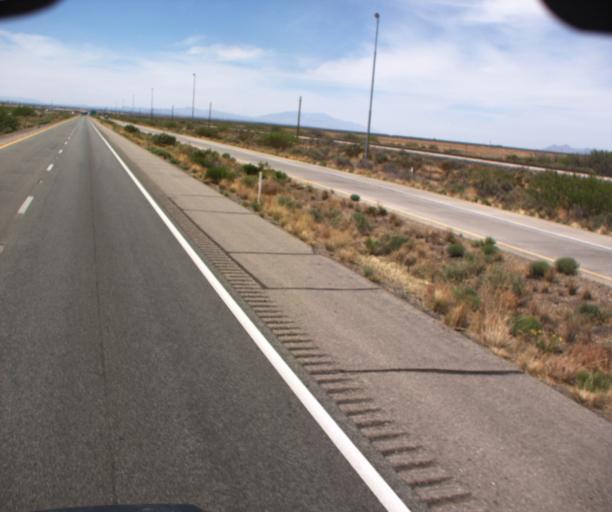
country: US
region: New Mexico
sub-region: Hidalgo County
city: Lordsburg
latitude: 32.2550
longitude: -109.1673
